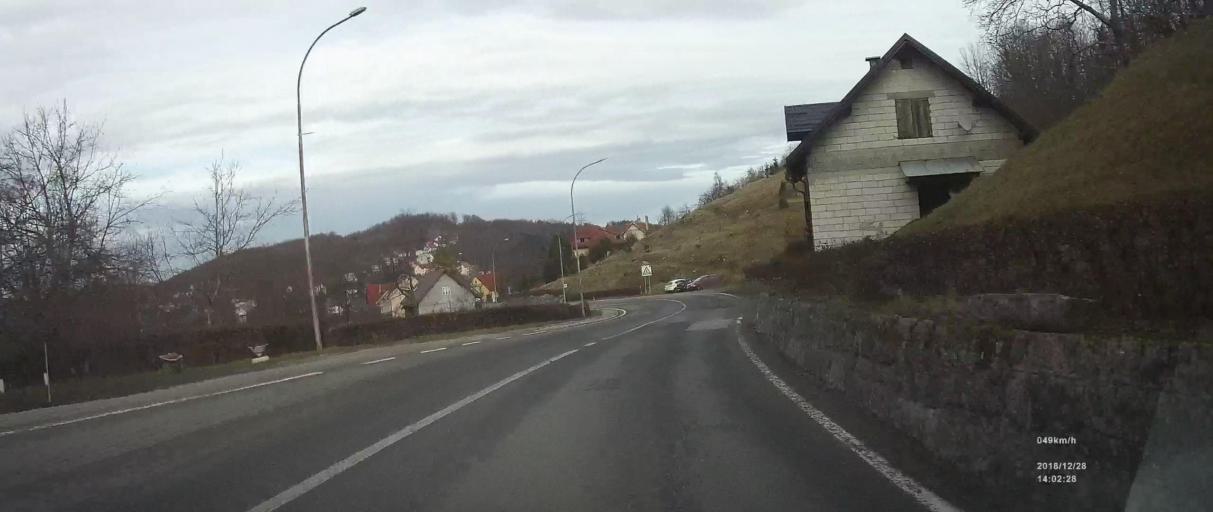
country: SI
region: Kostel
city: Kostel
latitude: 45.4294
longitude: 14.9036
